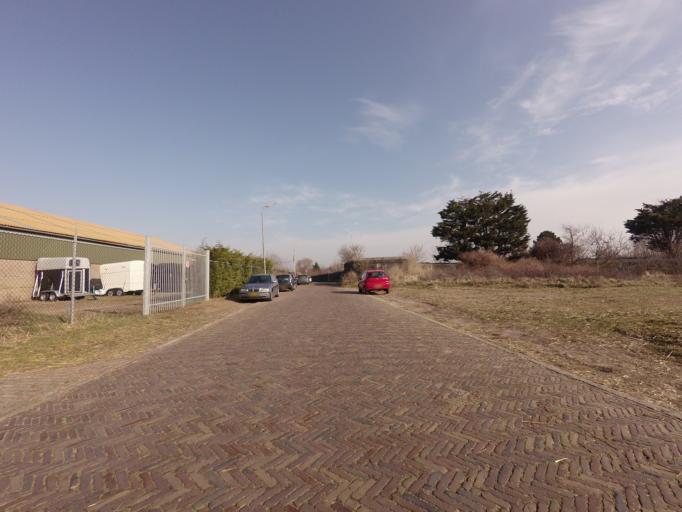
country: NL
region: North Holland
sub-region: Gemeente Zandvoort
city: Zandvoort
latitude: 52.3821
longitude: 4.5530
